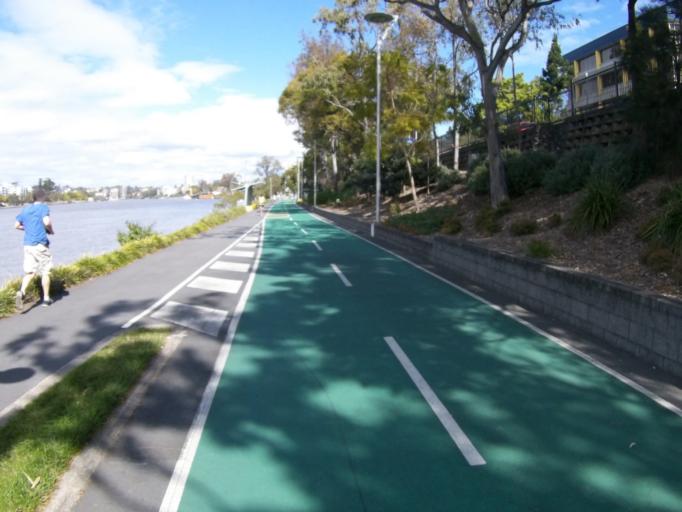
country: AU
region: Queensland
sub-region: Brisbane
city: Milton
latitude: -27.4779
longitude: 153.0004
